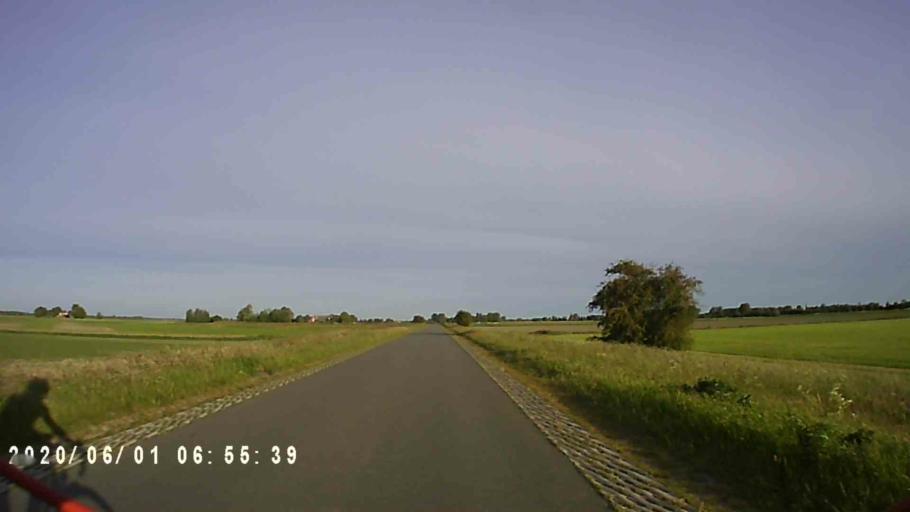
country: NL
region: Friesland
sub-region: Gemeente Kollumerland en Nieuwkruisland
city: Kollum
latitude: 53.3167
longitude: 6.1177
